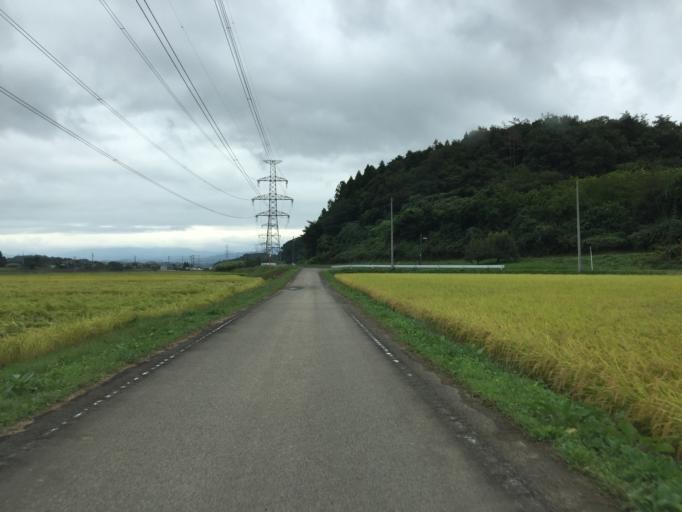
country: JP
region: Fukushima
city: Nihommatsu
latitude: 37.6477
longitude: 140.4458
